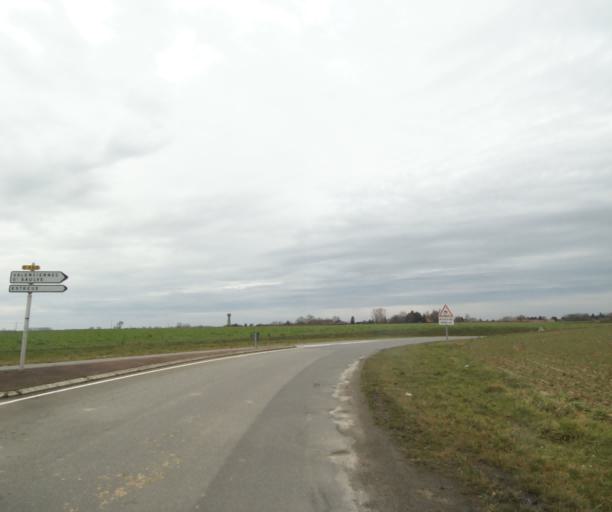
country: FR
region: Nord-Pas-de-Calais
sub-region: Departement du Nord
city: Curgies
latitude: 50.3549
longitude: 3.6096
